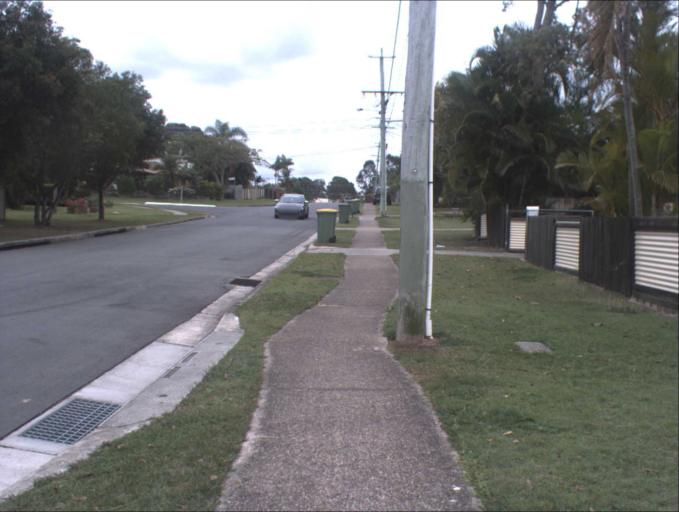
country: AU
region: Queensland
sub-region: Logan
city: Park Ridge South
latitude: -27.6813
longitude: 153.0222
